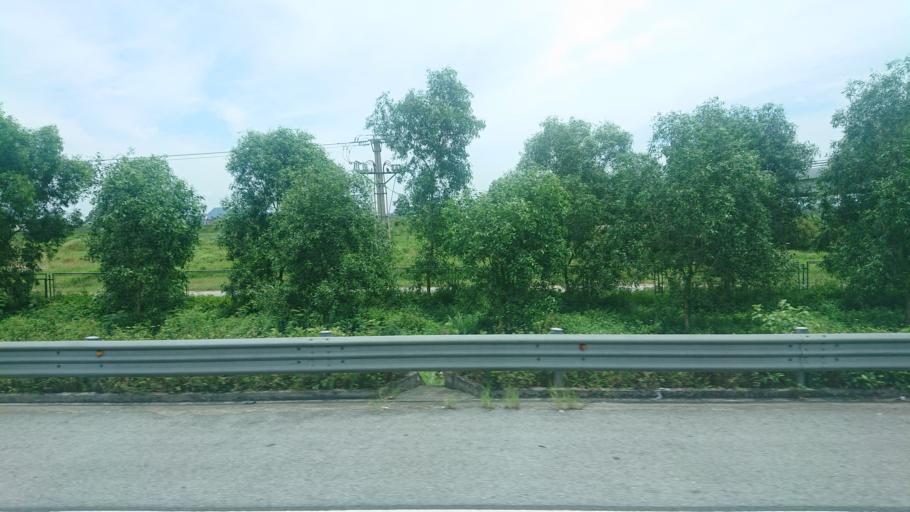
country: VN
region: Hai Phong
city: An Lao
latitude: 20.7880
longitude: 106.5573
